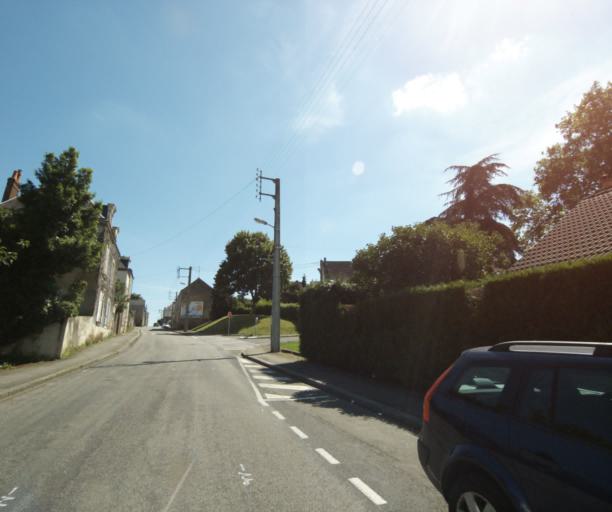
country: FR
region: Pays de la Loire
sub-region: Departement de la Mayenne
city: Laval
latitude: 48.0730
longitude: -0.7856
